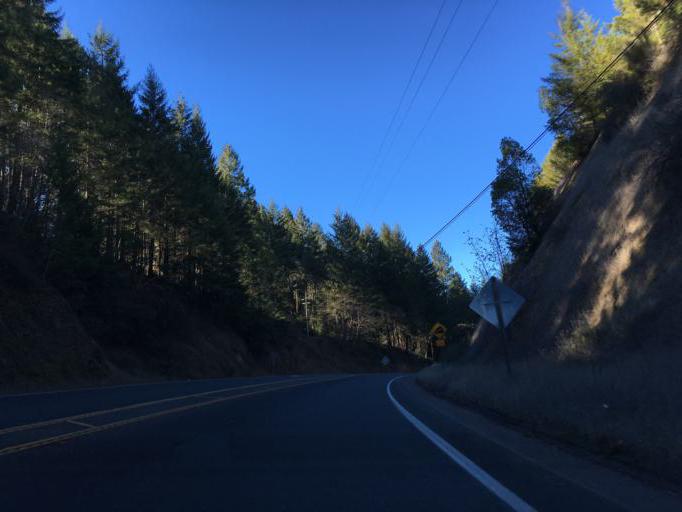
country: US
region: California
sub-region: Mendocino County
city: Brooktrails
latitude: 39.4711
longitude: -123.3621
